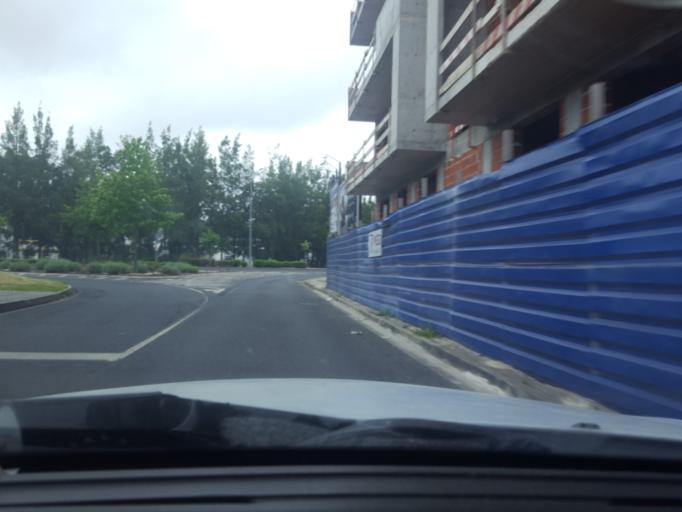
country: PT
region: Leiria
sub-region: Leiria
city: Leiria
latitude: 39.7362
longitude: -8.7938
